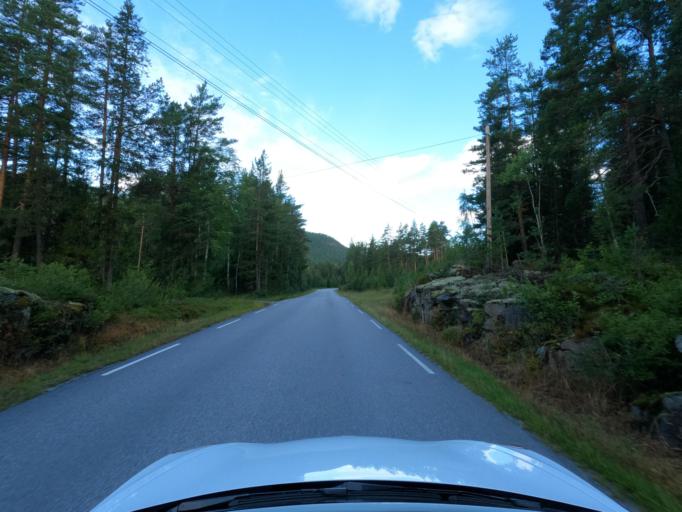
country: NO
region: Telemark
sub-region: Hjartdal
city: Sauland
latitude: 59.8167
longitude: 9.0721
